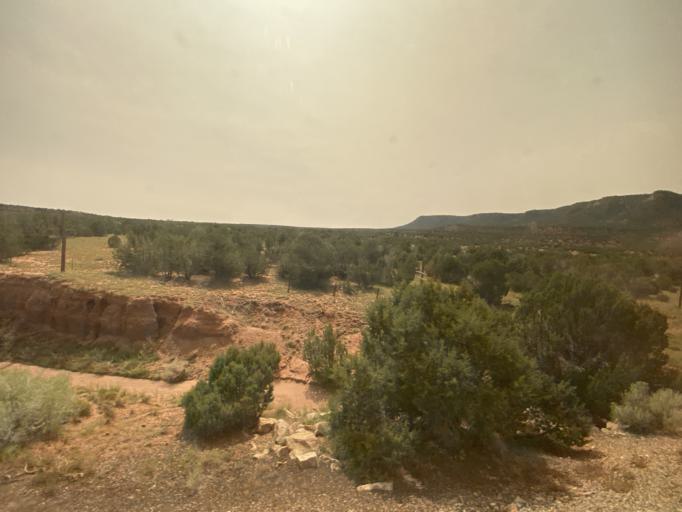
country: US
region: New Mexico
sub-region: San Miguel County
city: Pecos
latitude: 35.3939
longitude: -105.4858
